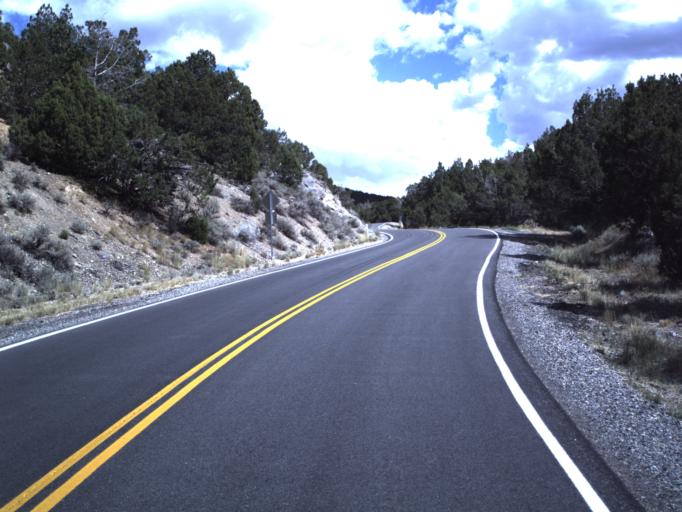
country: US
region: Utah
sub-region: Tooele County
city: Grantsville
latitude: 40.3461
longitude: -112.5886
